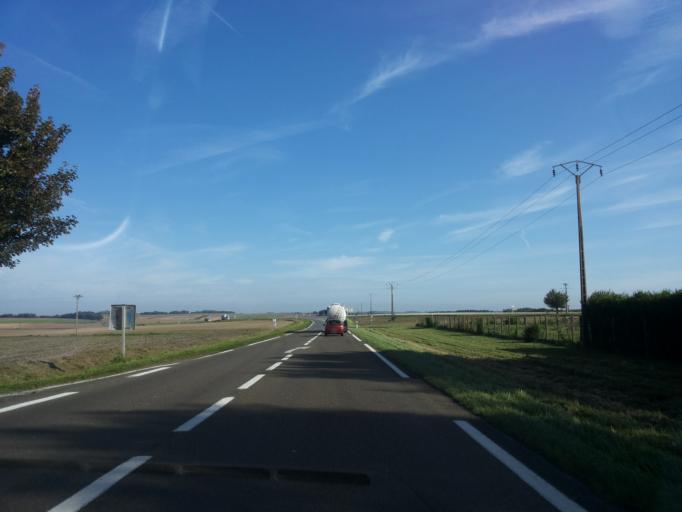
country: FR
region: Picardie
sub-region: Departement de l'Aisne
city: La Fere
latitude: 49.7218
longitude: 3.3470
